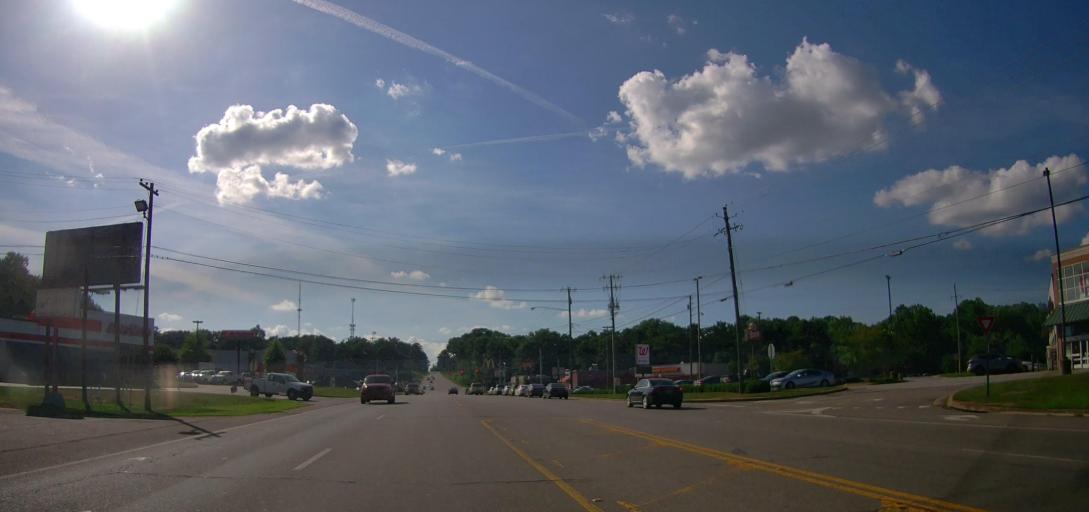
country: US
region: Alabama
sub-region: Tuscaloosa County
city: Holt
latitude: 33.1963
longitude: -87.4776
